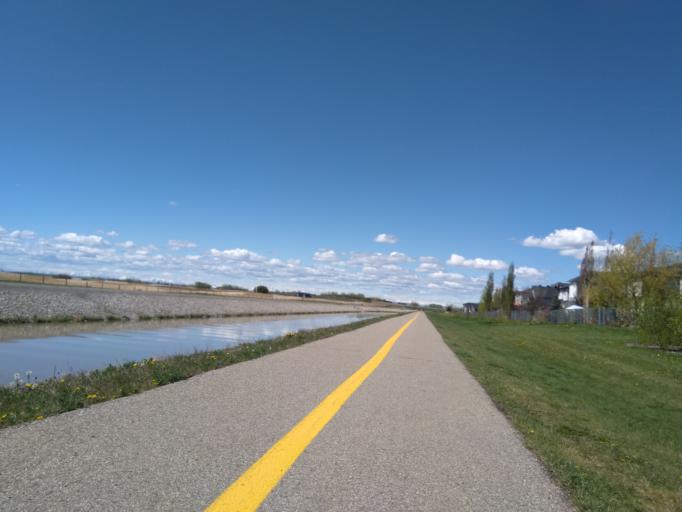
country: CA
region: Alberta
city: Chestermere
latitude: 51.0199
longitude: -113.8305
